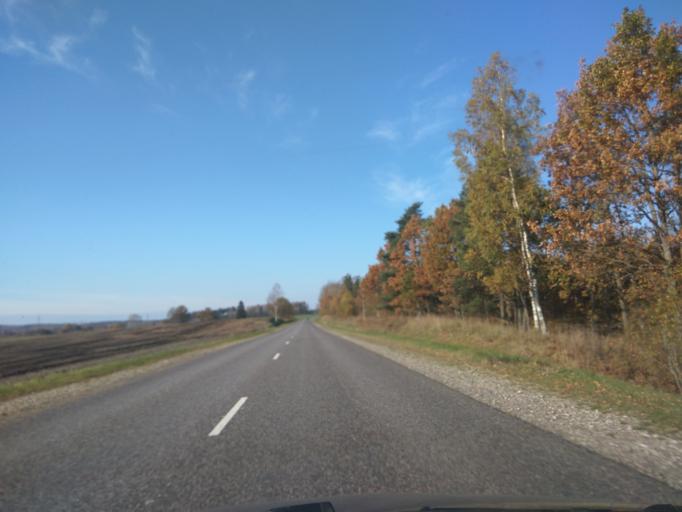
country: LV
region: Kuldigas Rajons
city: Kuldiga
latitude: 57.0289
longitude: 21.8520
